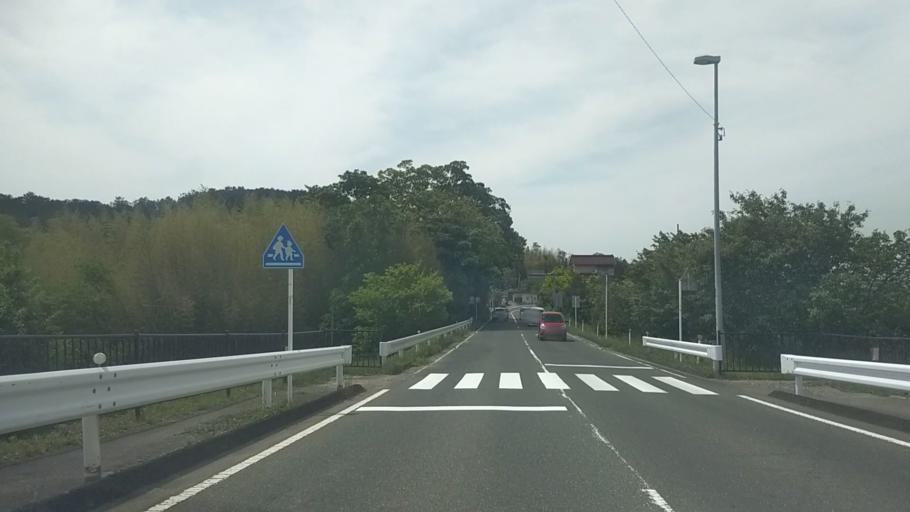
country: JP
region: Shizuoka
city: Kosai-shi
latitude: 34.7899
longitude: 137.5829
